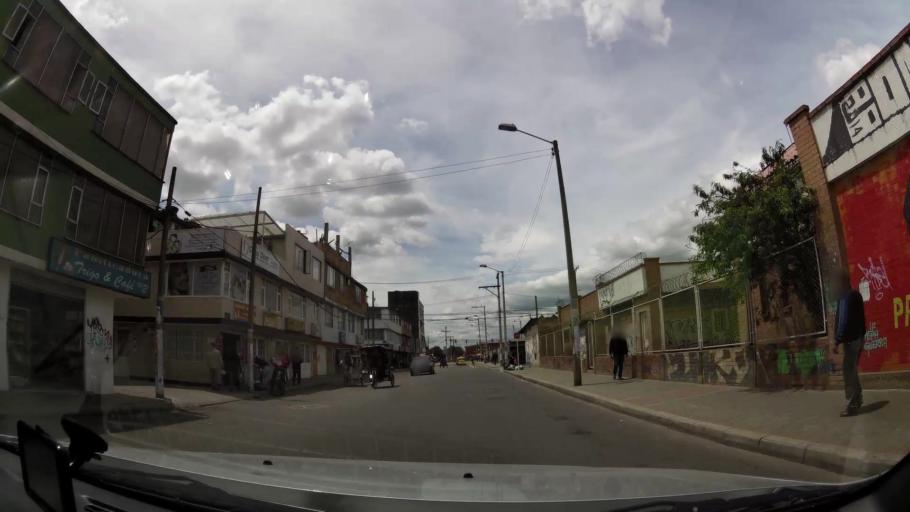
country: CO
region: Cundinamarca
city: Soacha
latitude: 4.6429
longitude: -74.1615
